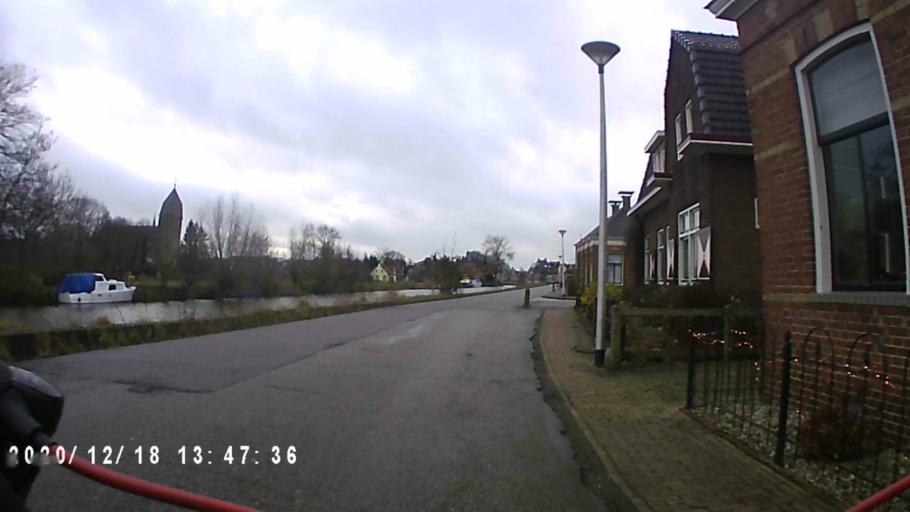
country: NL
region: Groningen
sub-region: Gemeente Bedum
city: Bedum
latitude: 53.3039
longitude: 6.6021
